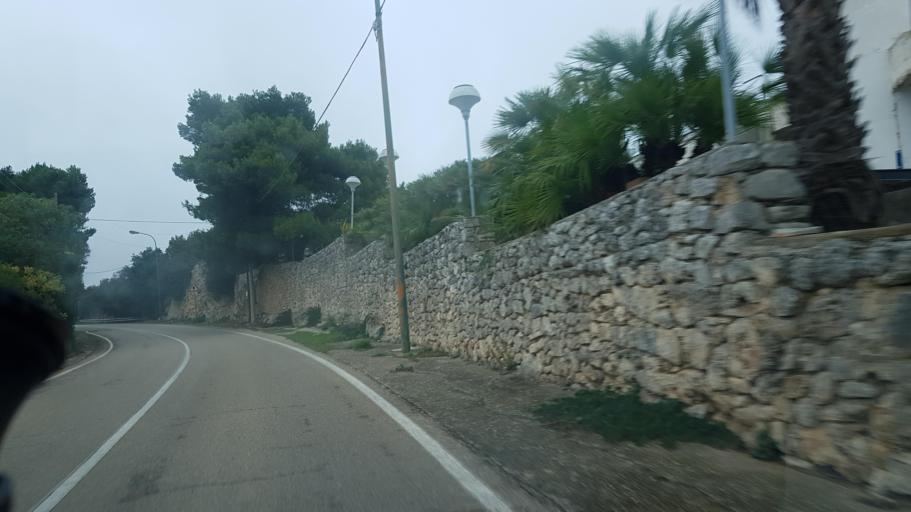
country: IT
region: Apulia
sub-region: Provincia di Brindisi
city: Ostuni
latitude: 40.7346
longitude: 17.5535
